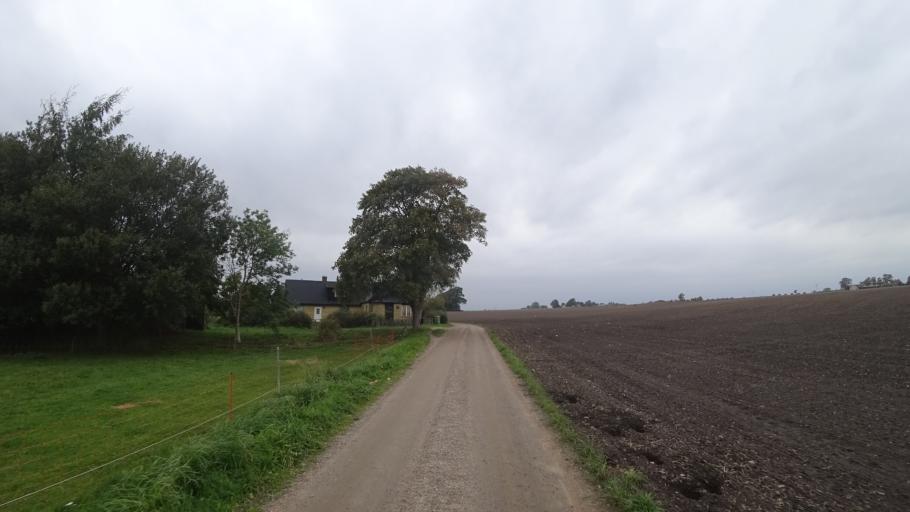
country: SE
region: Skane
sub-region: Kavlinge Kommun
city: Kaevlinge
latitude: 55.8011
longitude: 13.1372
